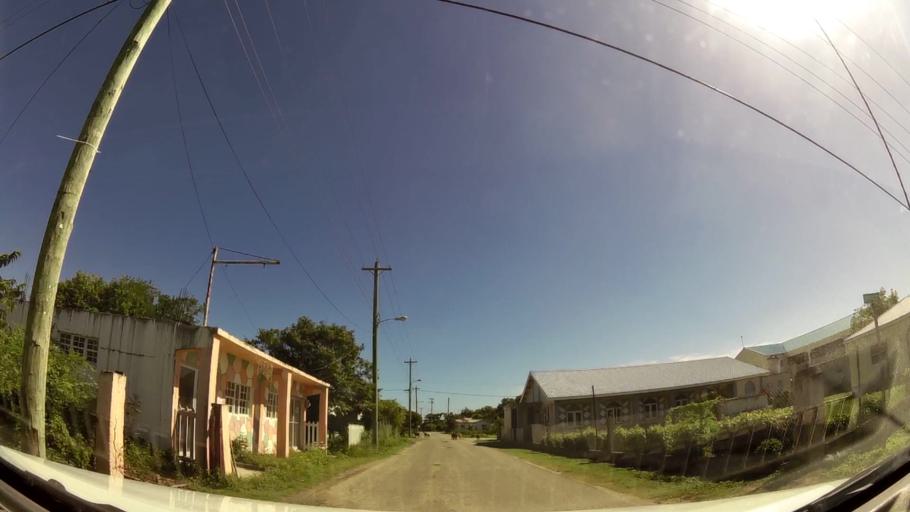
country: AG
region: Barbuda
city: Codrington
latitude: 17.6377
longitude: -61.8243
